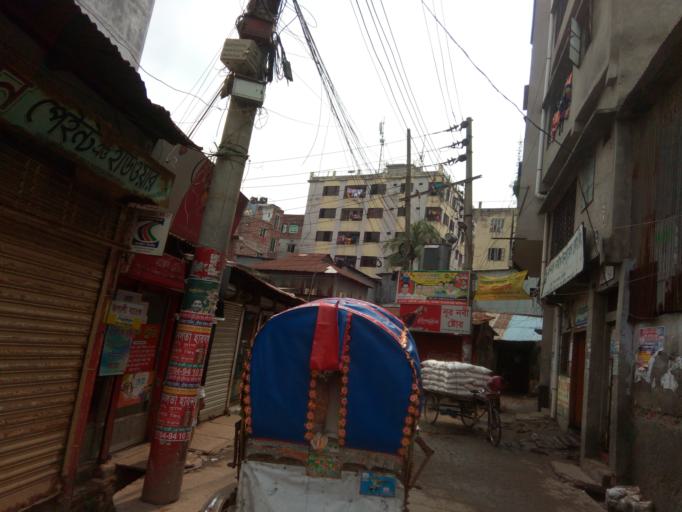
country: BD
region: Dhaka
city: Azimpur
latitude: 23.7169
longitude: 90.3889
